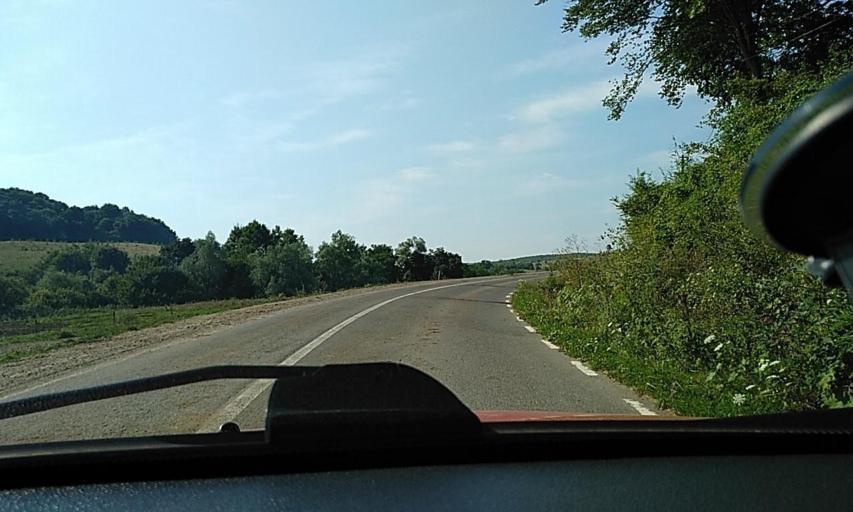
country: RO
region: Brasov
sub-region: Comuna Bunesti
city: Bunesti
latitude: 46.0952
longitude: 25.0581
